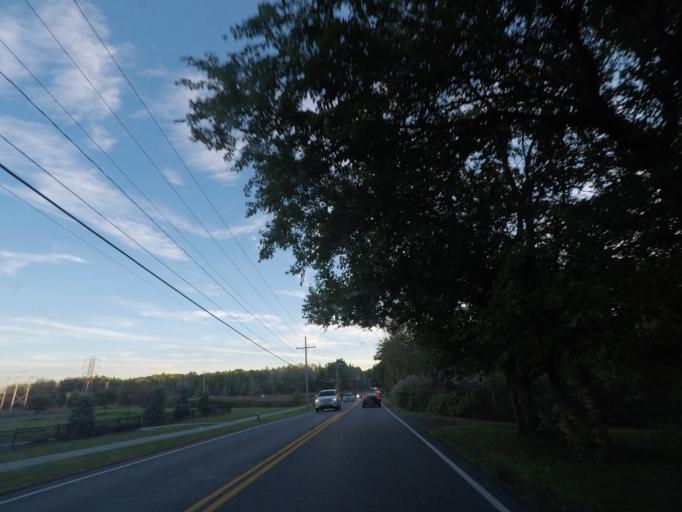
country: US
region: New York
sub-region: Albany County
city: Colonie
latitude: 42.7333
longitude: -73.8264
